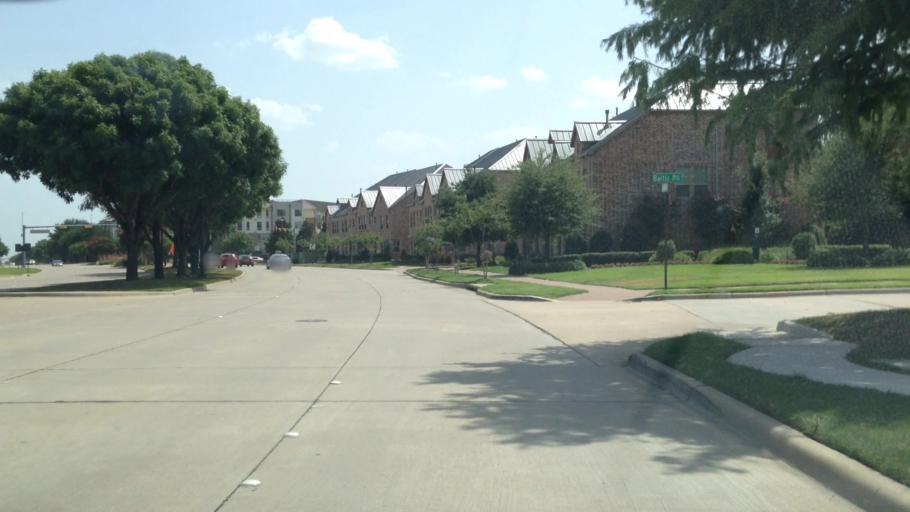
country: US
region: Texas
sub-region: Collin County
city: Frisco
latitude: 33.0857
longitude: -96.8183
